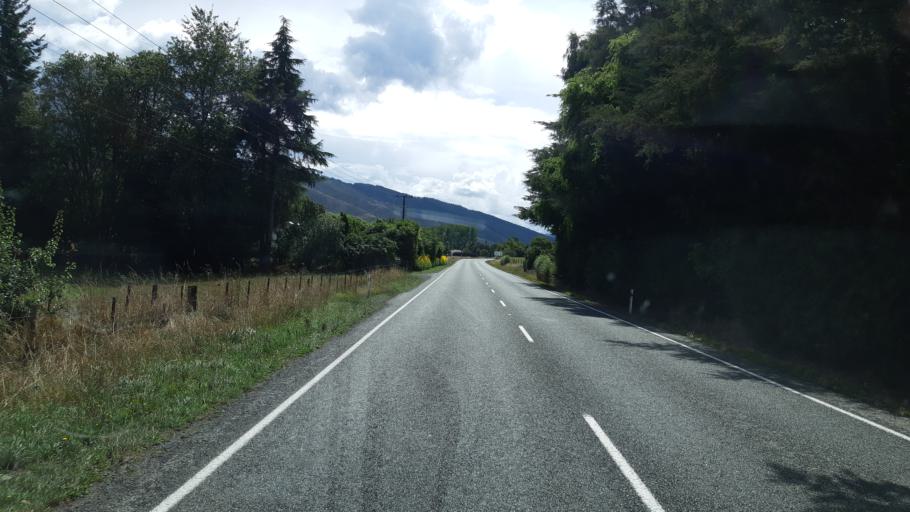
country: NZ
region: Tasman
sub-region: Tasman District
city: Wakefield
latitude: -41.4730
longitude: 172.8060
